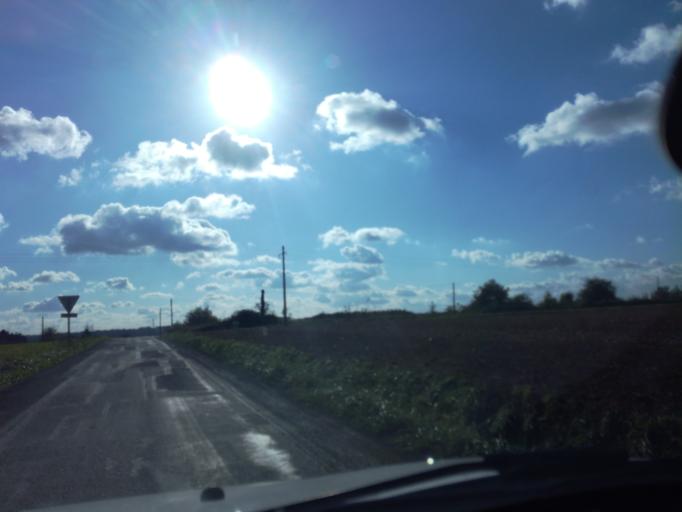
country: FR
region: Brittany
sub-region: Departement d'Ille-et-Vilaine
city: Chavagne
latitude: 48.0580
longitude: -1.7994
